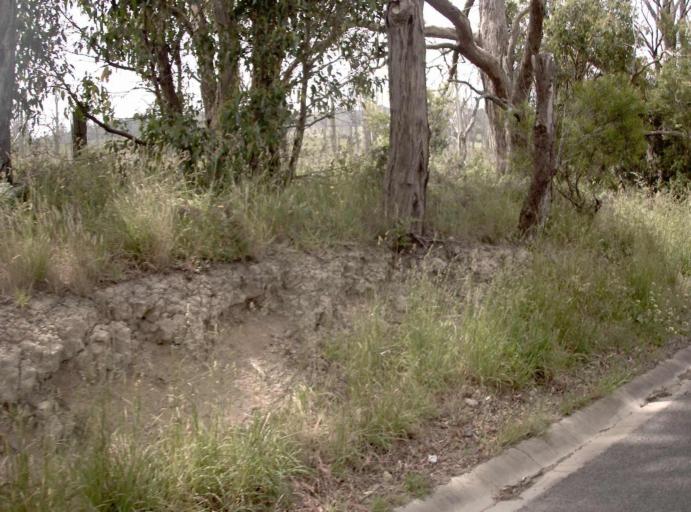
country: AU
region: Victoria
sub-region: Baw Baw
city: Warragul
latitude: -38.4380
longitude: 146.0356
